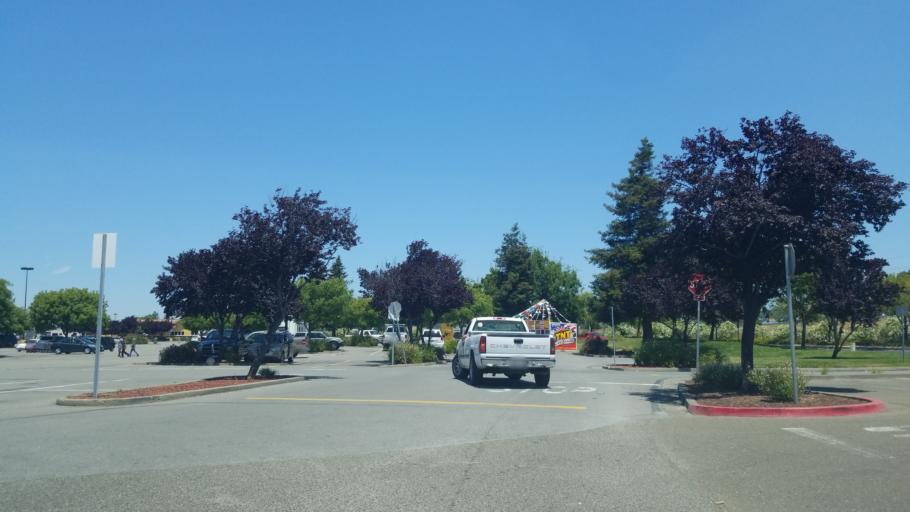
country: US
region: California
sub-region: Sonoma County
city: Rohnert Park
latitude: 38.3666
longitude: -122.7143
